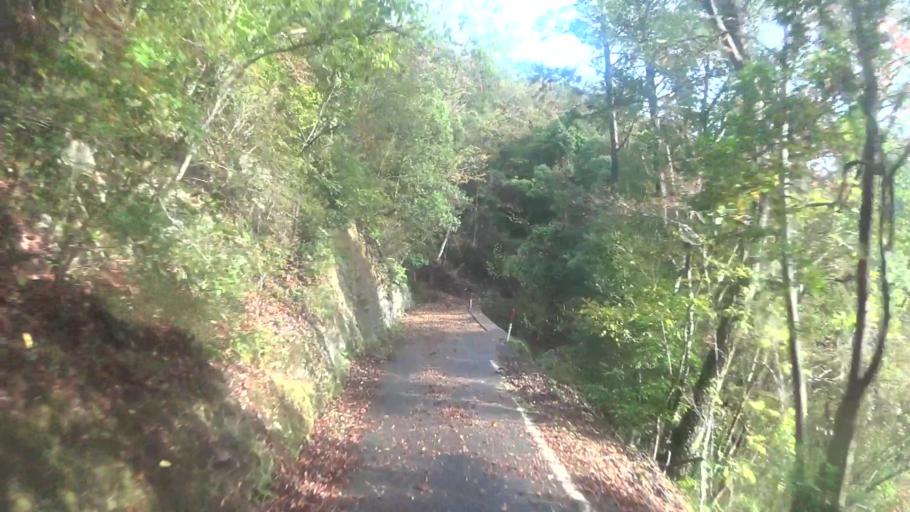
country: JP
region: Kyoto
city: Ayabe
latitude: 35.2693
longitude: 135.2266
